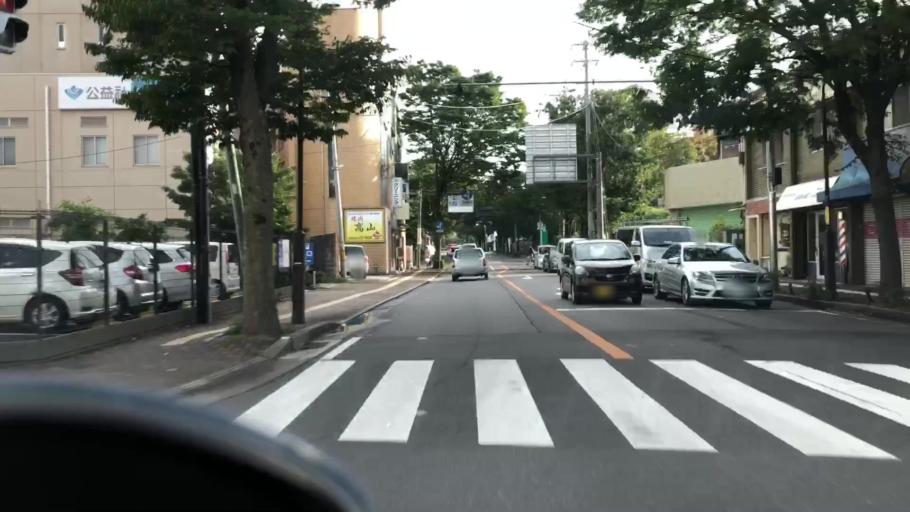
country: JP
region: Hyogo
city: Takarazuka
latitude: 34.8043
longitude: 135.3634
